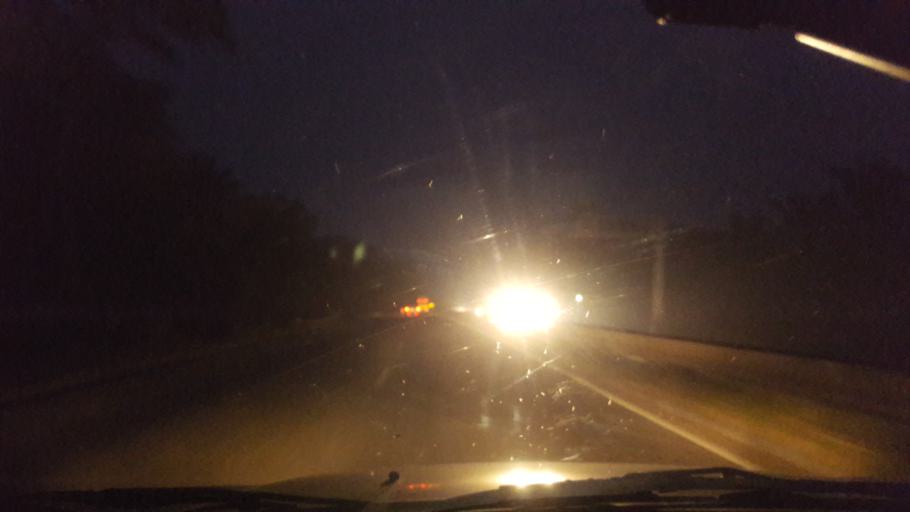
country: IN
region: Andhra Pradesh
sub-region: East Godavari
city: Peddapuram
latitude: 17.1375
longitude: 81.9632
